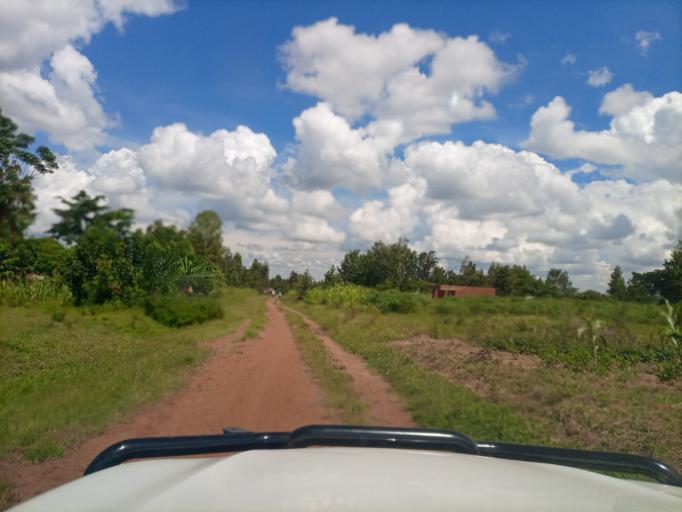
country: UG
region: Eastern Region
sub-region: Tororo District
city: Tororo
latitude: 0.7230
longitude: 34.0207
